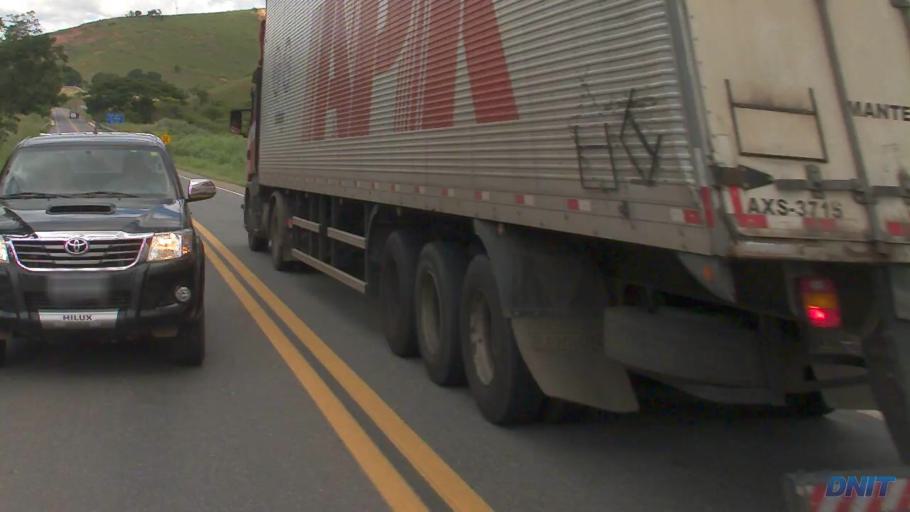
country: BR
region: Minas Gerais
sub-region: Governador Valadares
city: Governador Valadares
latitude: -18.9594
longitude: -42.0759
